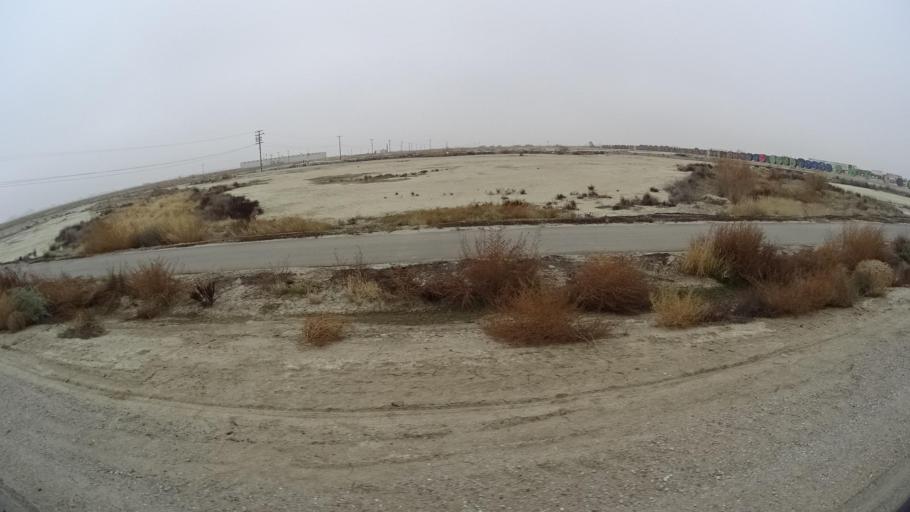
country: US
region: California
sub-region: Kern County
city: Rosedale
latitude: 35.2484
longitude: -119.2527
